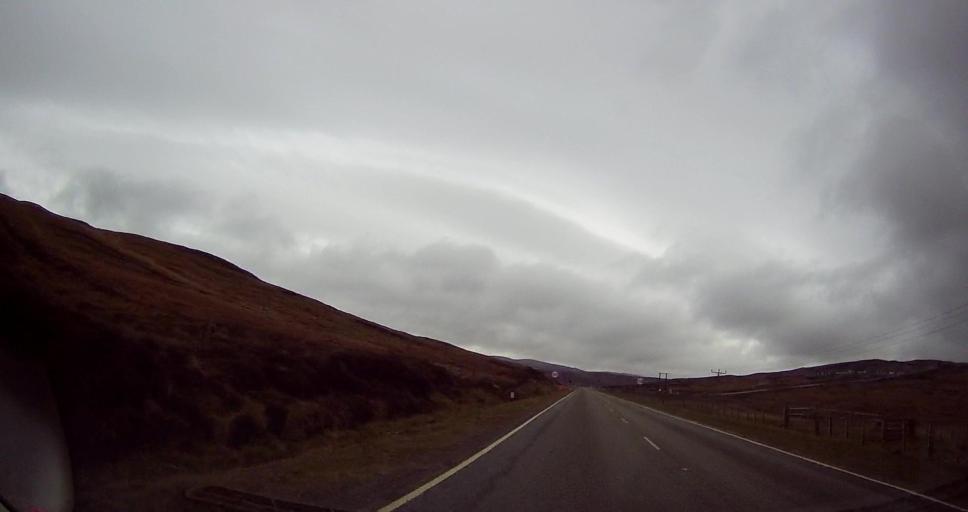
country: GB
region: Scotland
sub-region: Shetland Islands
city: Lerwick
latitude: 60.2701
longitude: -1.2351
